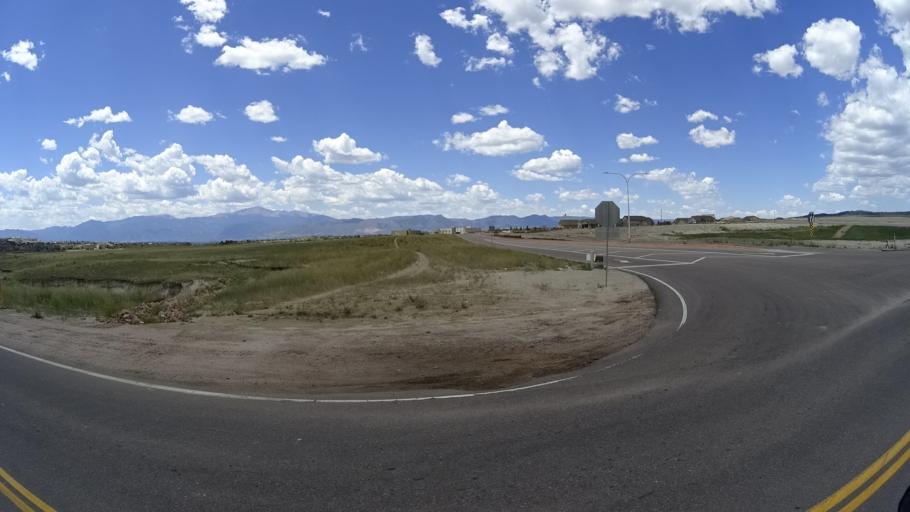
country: US
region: Colorado
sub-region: El Paso County
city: Black Forest
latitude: 38.9578
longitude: -104.7007
